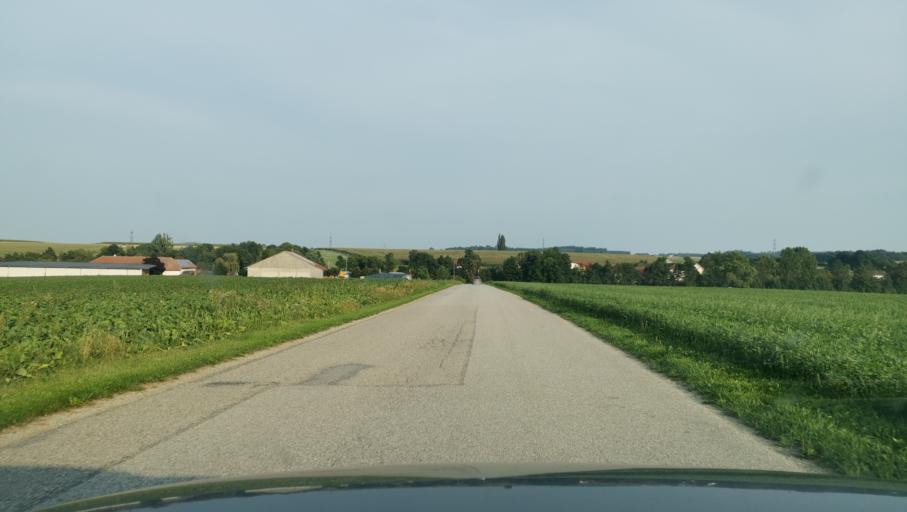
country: AT
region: Upper Austria
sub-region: Politischer Bezirk Grieskirchen
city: Grieskirchen
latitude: 48.2900
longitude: 13.8055
